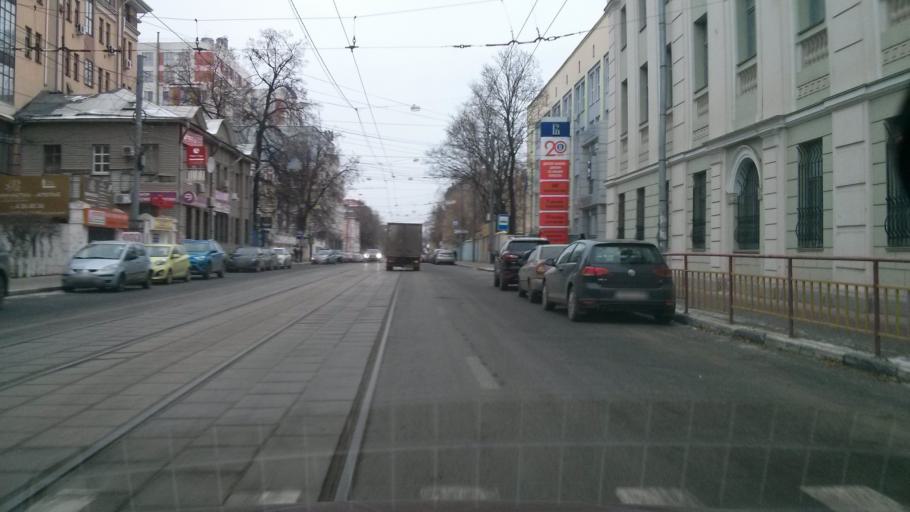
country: RU
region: Nizjnij Novgorod
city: Nizhniy Novgorod
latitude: 56.3253
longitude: 44.0209
